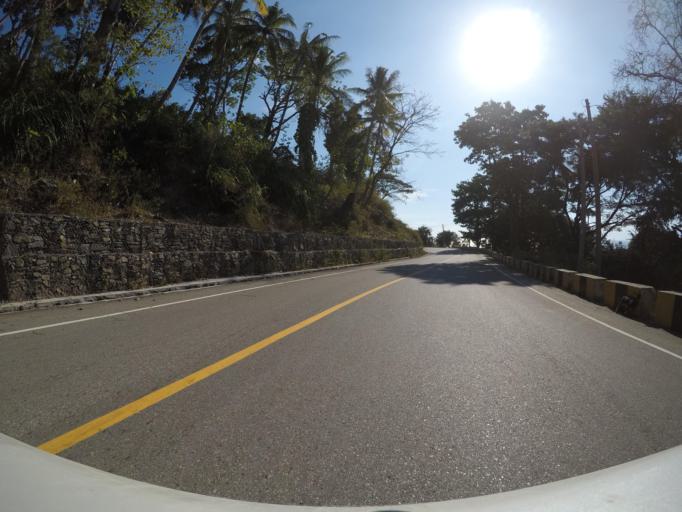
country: TL
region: Liquica
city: Maubara
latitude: -8.6528
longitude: 125.1198
